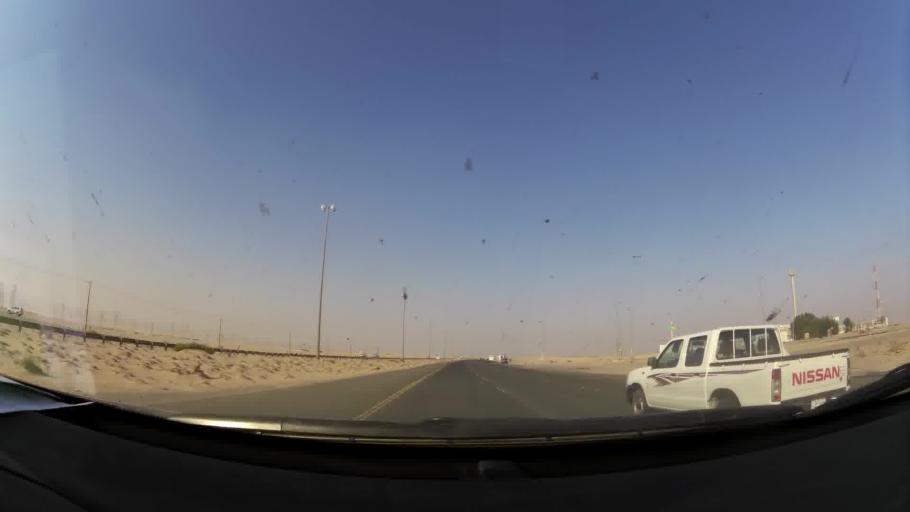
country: KW
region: Muhafazat al Jahra'
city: Al Jahra'
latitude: 29.6925
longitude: 47.6671
